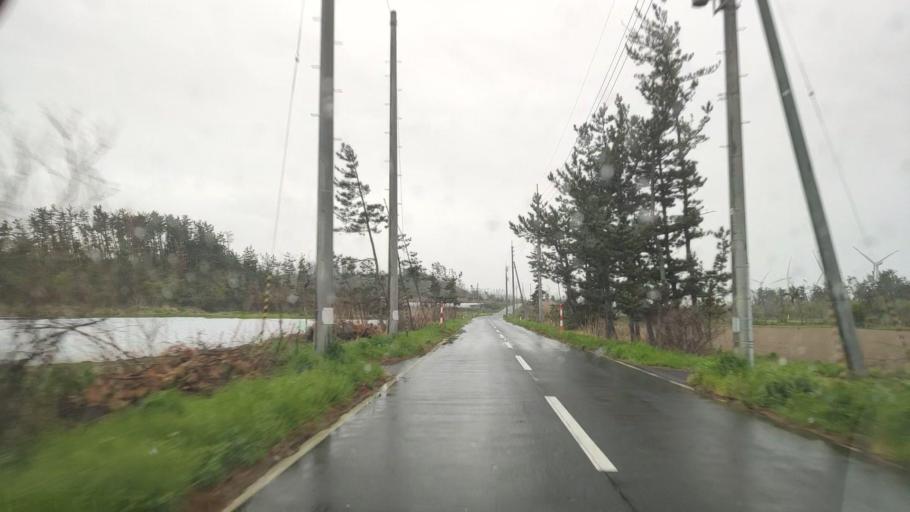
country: JP
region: Akita
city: Noshiromachi
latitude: 40.0919
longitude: 139.9615
